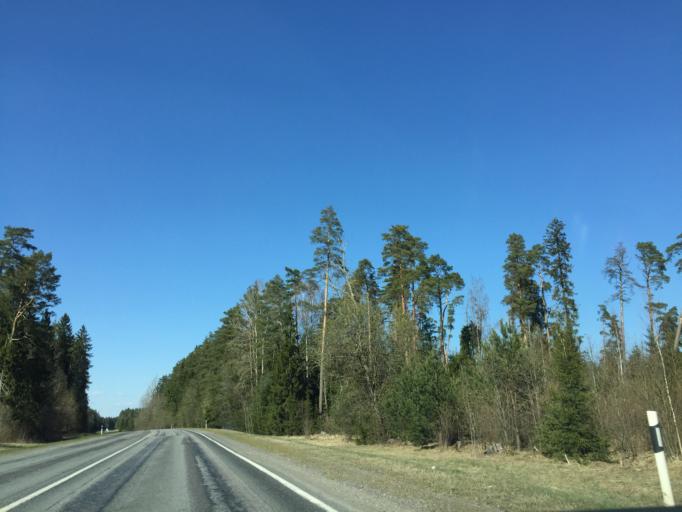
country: EE
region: Viljandimaa
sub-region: Viljandi linn
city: Viljandi
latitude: 58.2890
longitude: 25.5818
